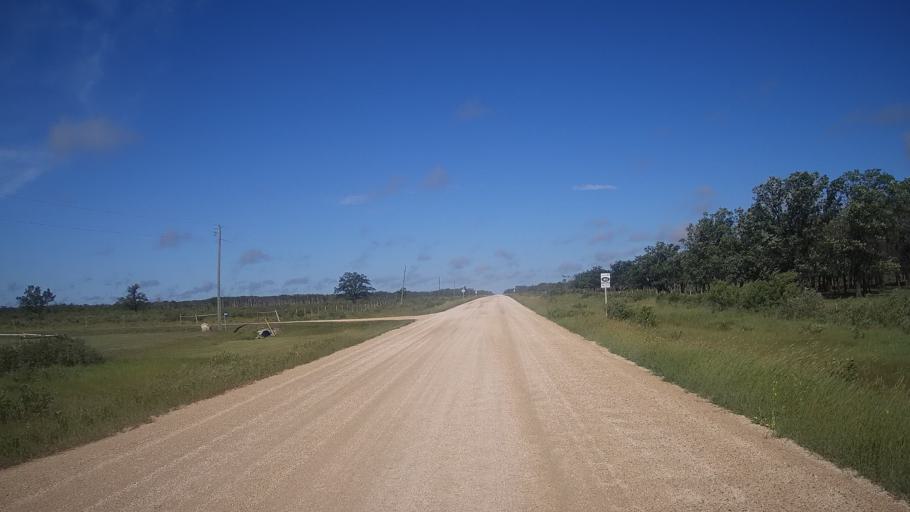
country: CA
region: Manitoba
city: Stonewall
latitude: 50.2411
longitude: -97.7367
